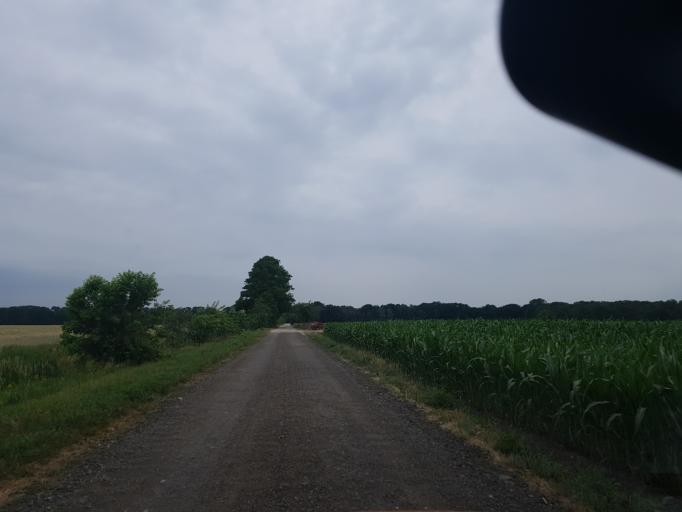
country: DE
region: Brandenburg
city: Schonewalde
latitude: 51.6949
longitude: 13.5424
